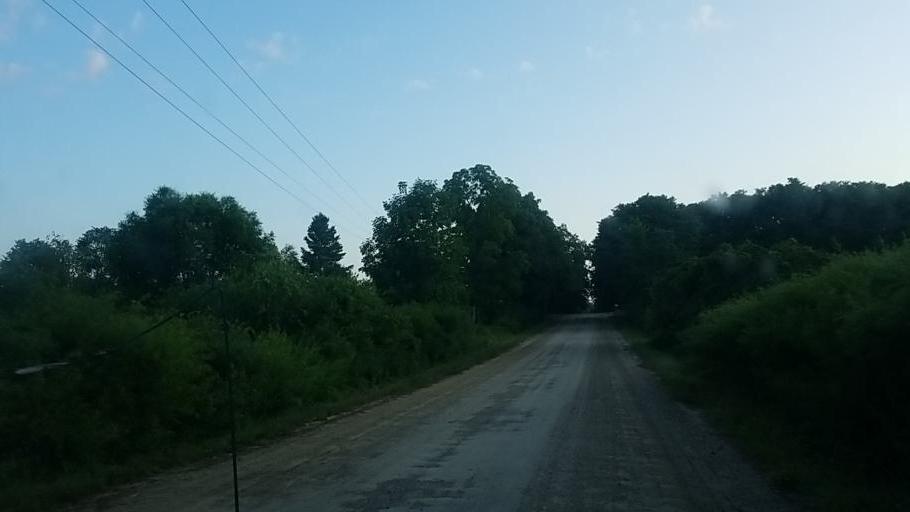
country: US
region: Michigan
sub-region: Osceola County
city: Evart
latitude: 43.9076
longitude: -85.2065
